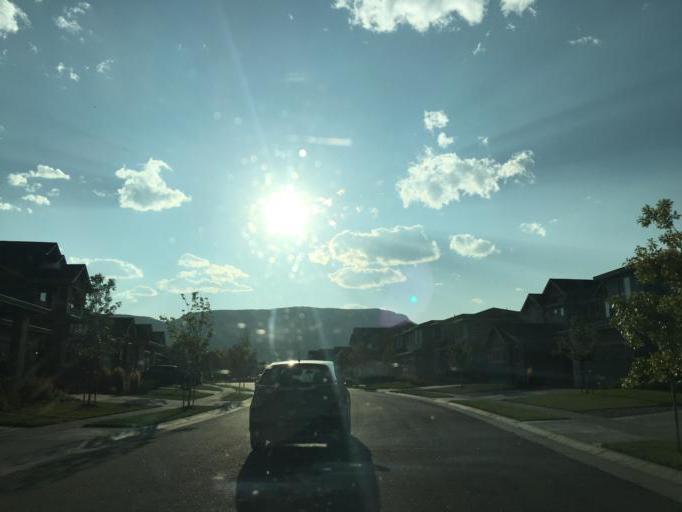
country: US
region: Colorado
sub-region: Jefferson County
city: Applewood
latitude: 39.7876
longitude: -105.1717
